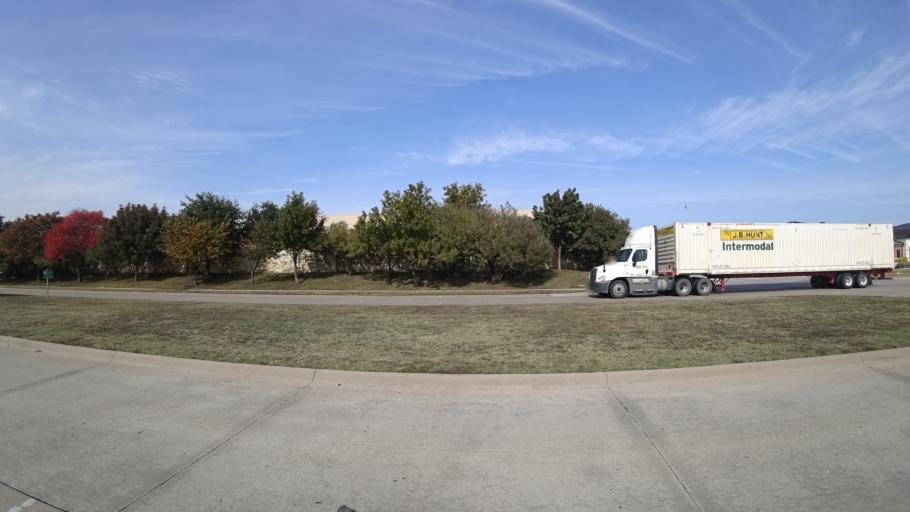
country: US
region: Texas
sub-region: Denton County
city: The Colony
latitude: 33.0632
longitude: -96.8834
